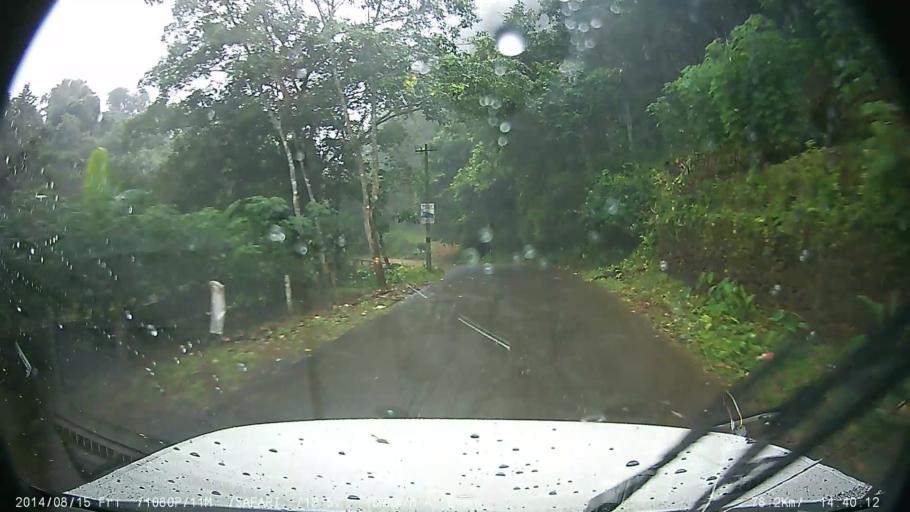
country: IN
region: Kerala
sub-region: Kottayam
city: Lalam
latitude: 9.8121
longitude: 76.7281
